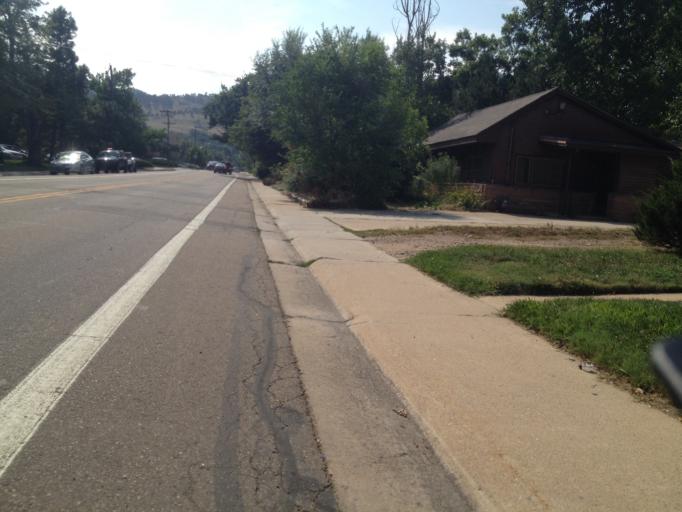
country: US
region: Colorado
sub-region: Boulder County
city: Boulder
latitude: 40.0268
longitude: -105.2790
